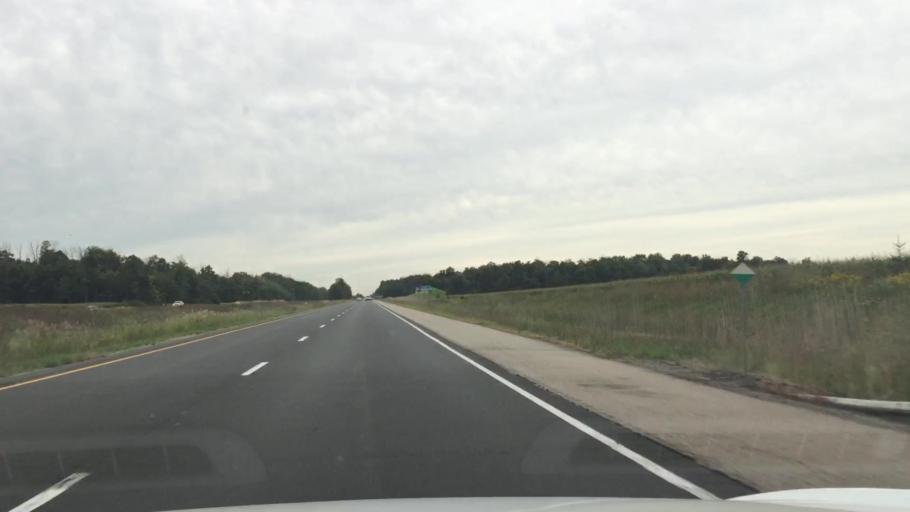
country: CA
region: Ontario
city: Lambton Shores
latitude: 42.9924
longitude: -81.8346
